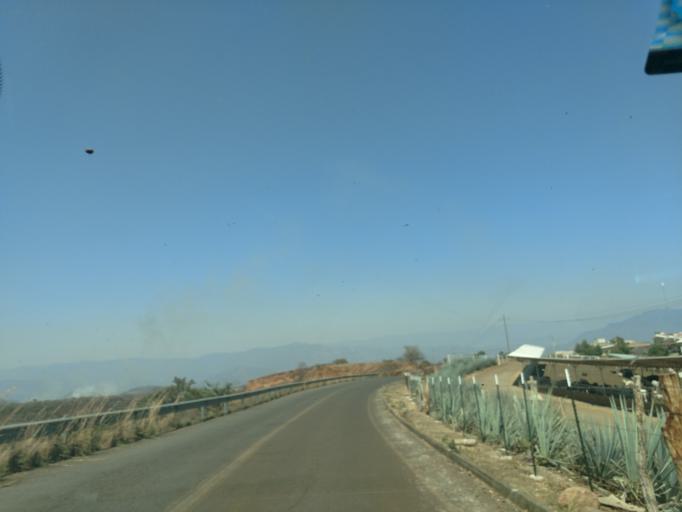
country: MX
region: Nayarit
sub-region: Tepic
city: La Corregidora
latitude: 21.4931
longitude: -104.6885
